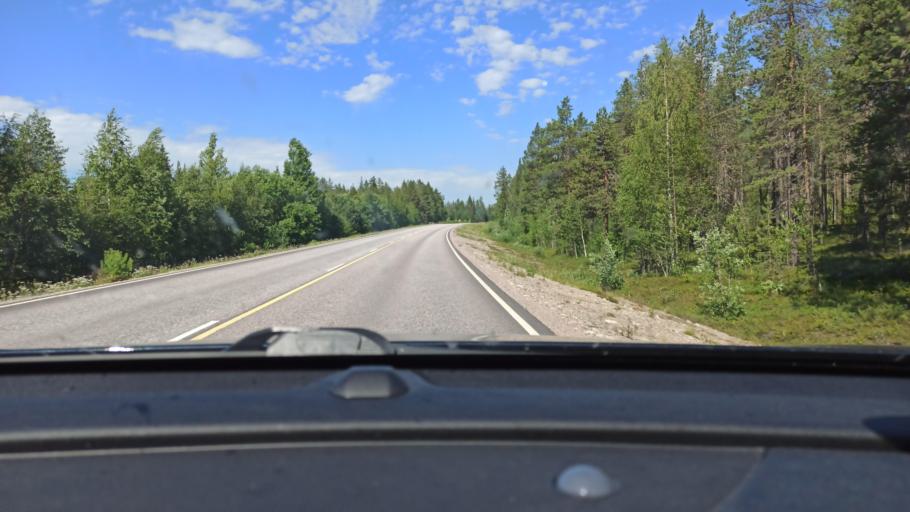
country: FI
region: Lapland
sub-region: Tunturi-Lappi
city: Muonio
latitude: 67.9947
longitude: 23.6200
